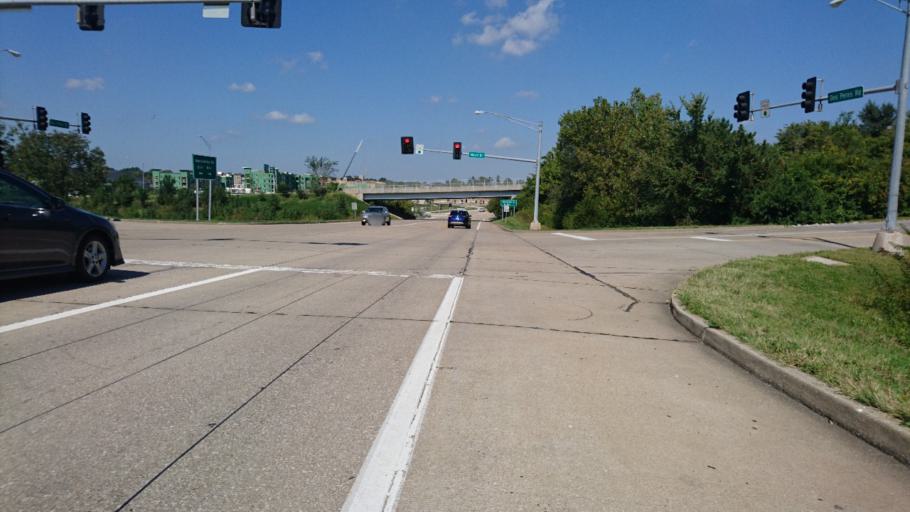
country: US
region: Missouri
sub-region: Saint Louis County
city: Town and Country
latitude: 38.6027
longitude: -90.4551
